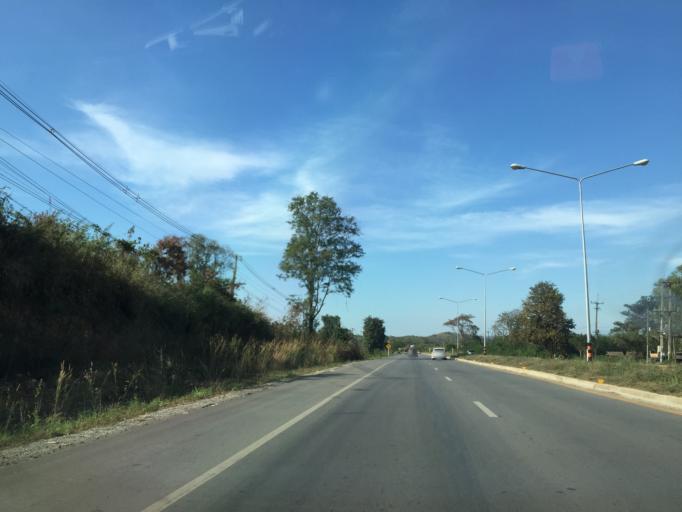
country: TH
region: Loei
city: Wang Saphung
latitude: 17.3008
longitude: 101.8092
